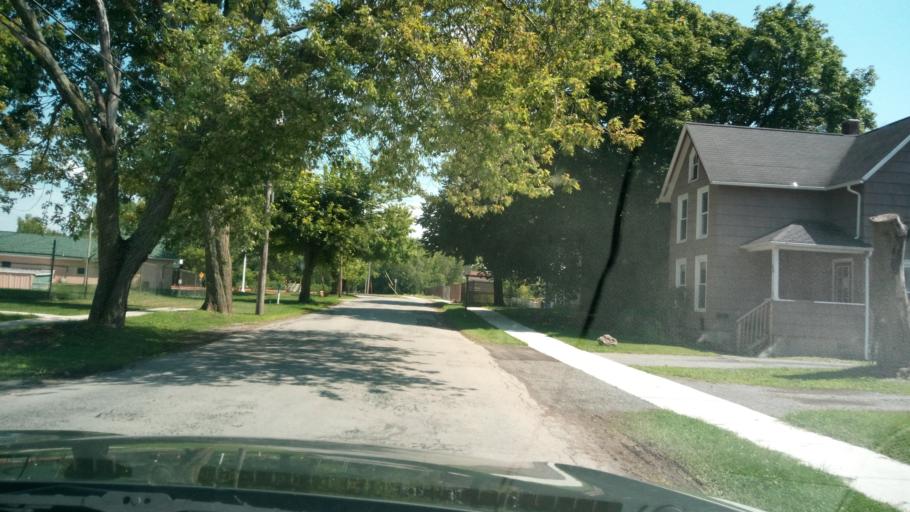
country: US
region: New York
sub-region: Genesee County
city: Batavia
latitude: 42.9880
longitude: -78.1655
